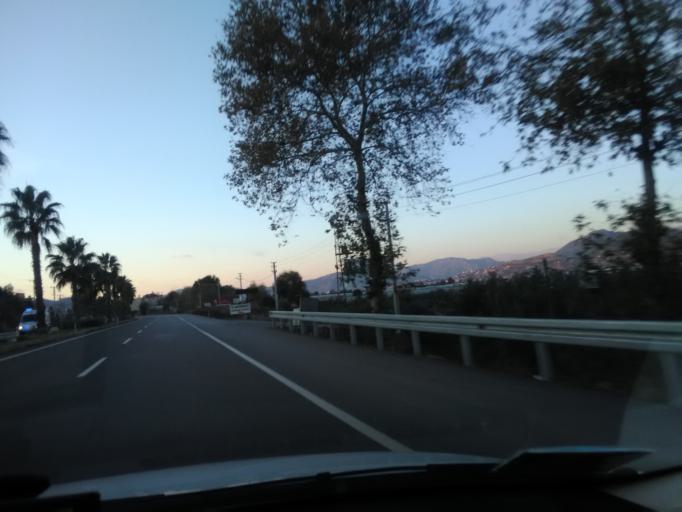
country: TR
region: Antalya
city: Gazipasa
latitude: 36.2522
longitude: 32.3375
